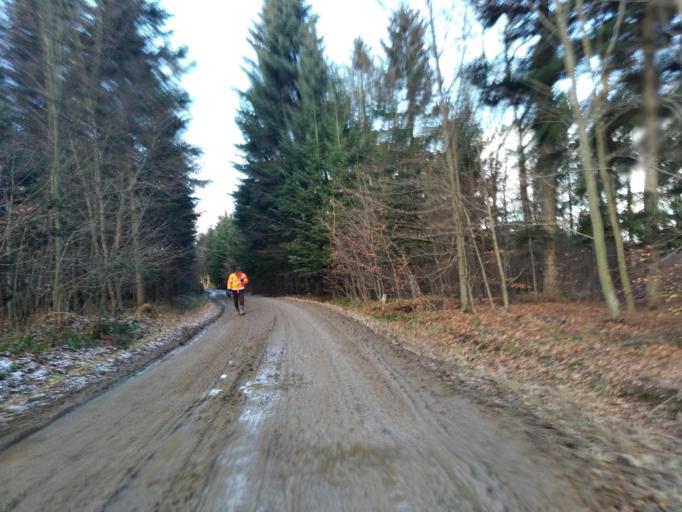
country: PL
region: Subcarpathian Voivodeship
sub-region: Powiat strzyzowski
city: Babica
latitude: 49.9512
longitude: 21.8703
